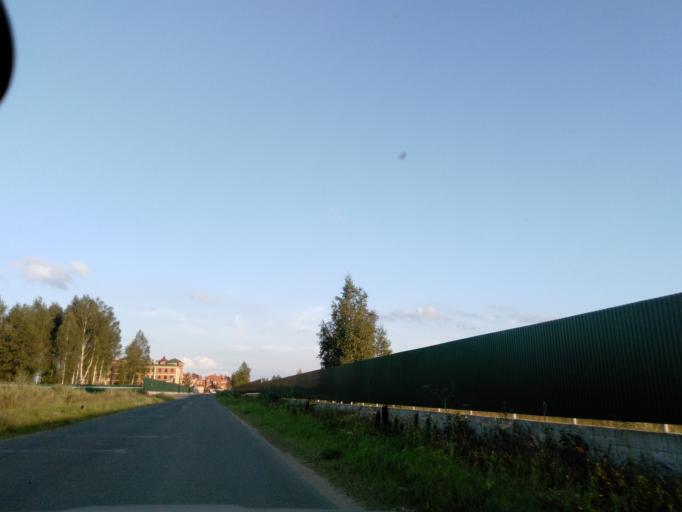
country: RU
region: Tverskaya
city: Konakovo
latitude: 56.6789
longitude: 36.7080
